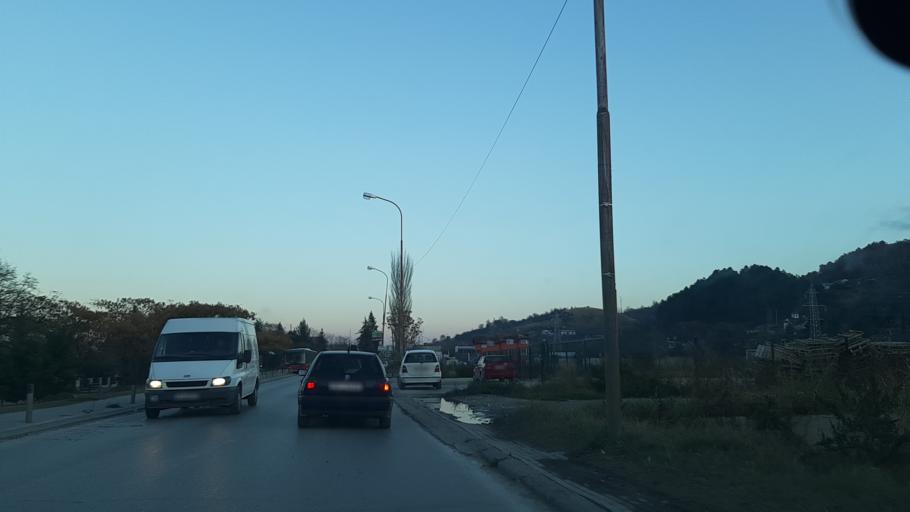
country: MK
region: Kisela Voda
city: Kisela Voda
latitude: 41.9385
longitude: 21.5080
